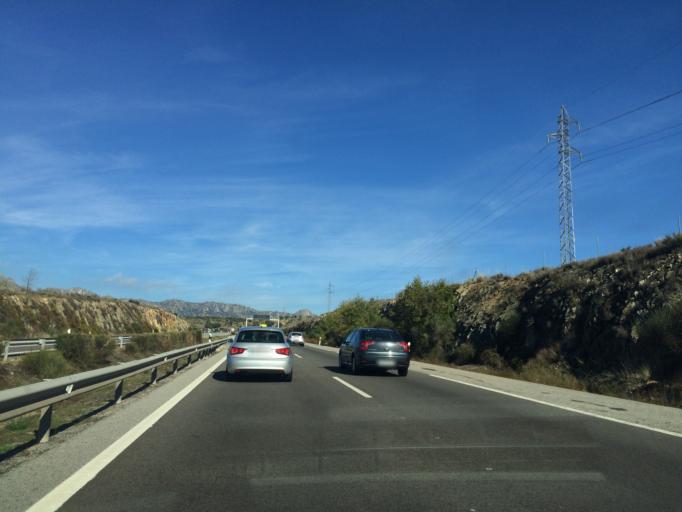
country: ES
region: Madrid
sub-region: Provincia de Madrid
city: Cabanillas de la Sierra
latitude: 40.8267
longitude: -3.6142
